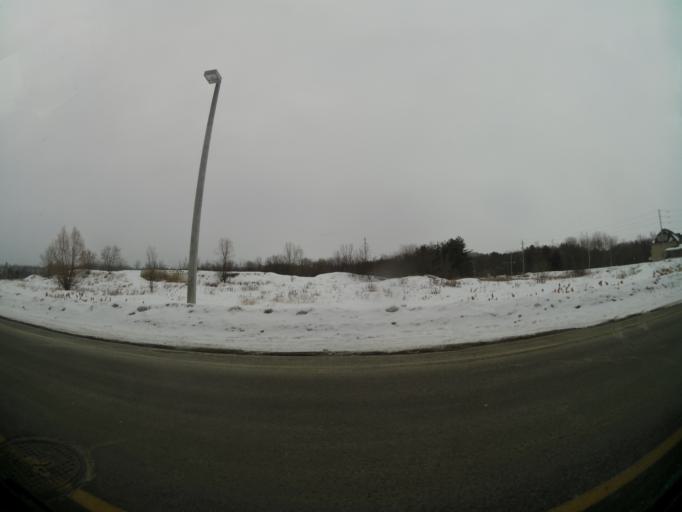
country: CA
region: Ontario
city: Clarence-Rockland
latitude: 45.4925
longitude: -75.4740
